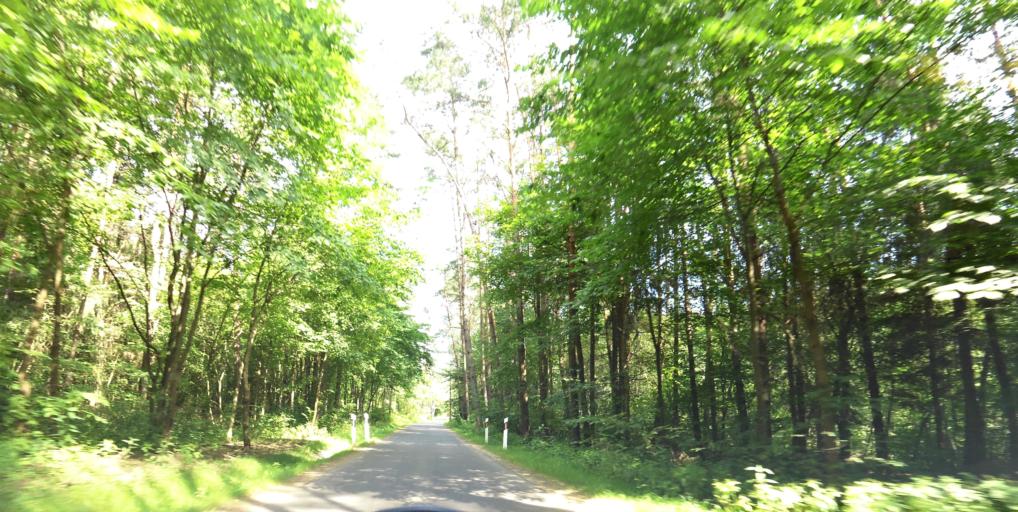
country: LT
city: Grigiskes
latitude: 54.7274
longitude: 25.0642
